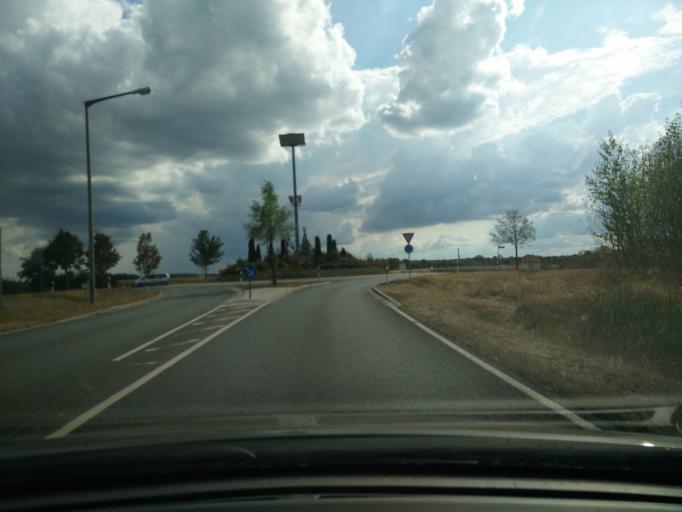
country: DE
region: Bavaria
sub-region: Regierungsbezirk Mittelfranken
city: Stein
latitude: 49.4034
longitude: 10.9979
